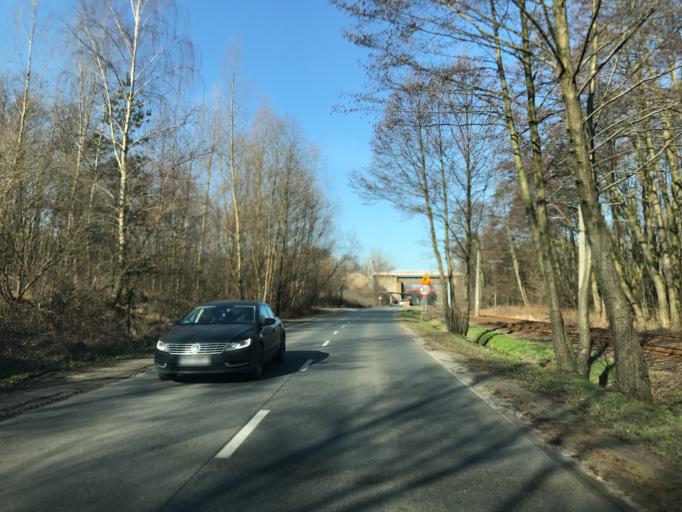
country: PL
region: Kujawsko-Pomorskie
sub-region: Powiat bydgoski
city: Osielsko
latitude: 53.1152
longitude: 18.1031
